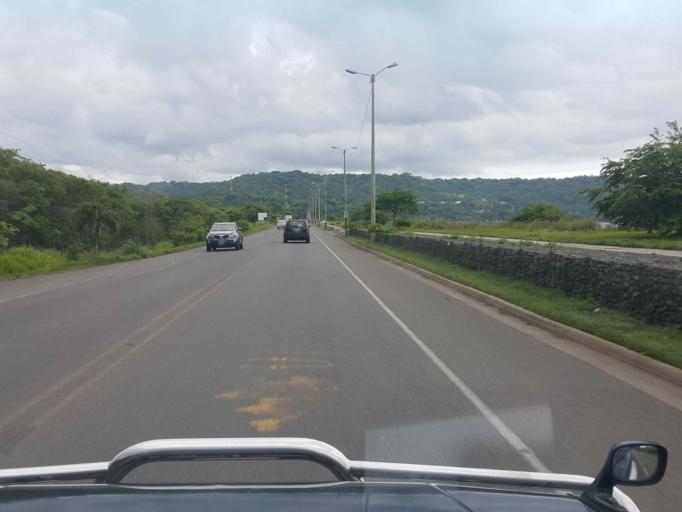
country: CR
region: Puntarenas
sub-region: Canton Central de Puntarenas
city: Chacarita
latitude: 9.9305
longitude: -84.7187
